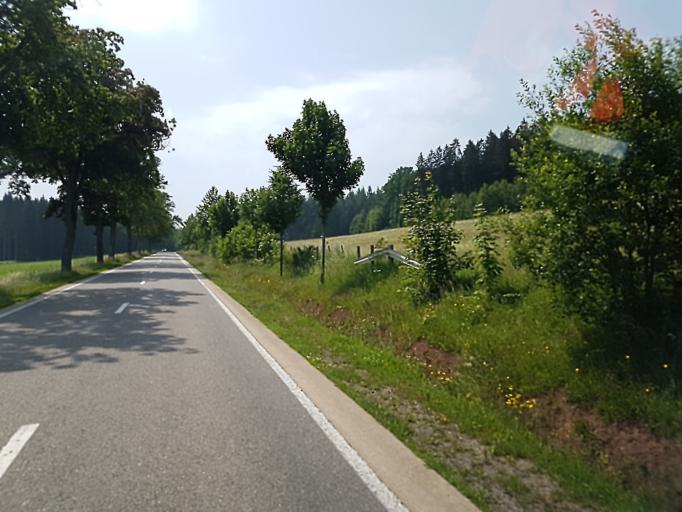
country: BE
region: Wallonia
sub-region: Province de Liege
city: Trois-Ponts
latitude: 50.3486
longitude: 5.8180
